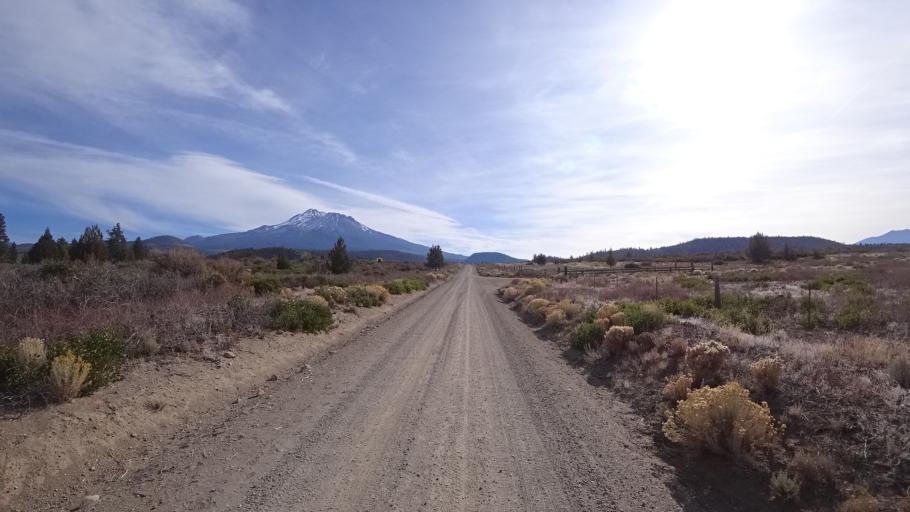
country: US
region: California
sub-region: Siskiyou County
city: Weed
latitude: 41.4889
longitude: -122.3701
